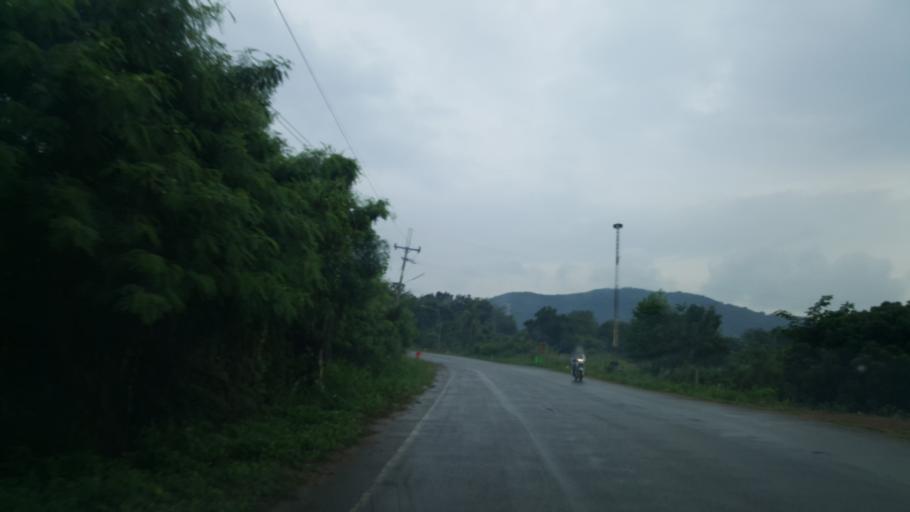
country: TH
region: Chon Buri
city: Sattahip
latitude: 12.7196
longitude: 100.9178
